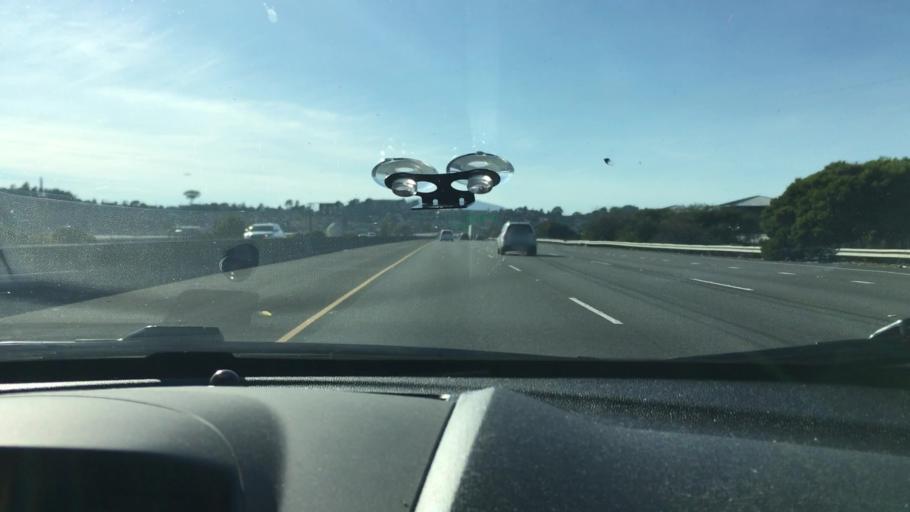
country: US
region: California
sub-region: Contra Costa County
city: Richmond
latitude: 37.9272
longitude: -122.3704
